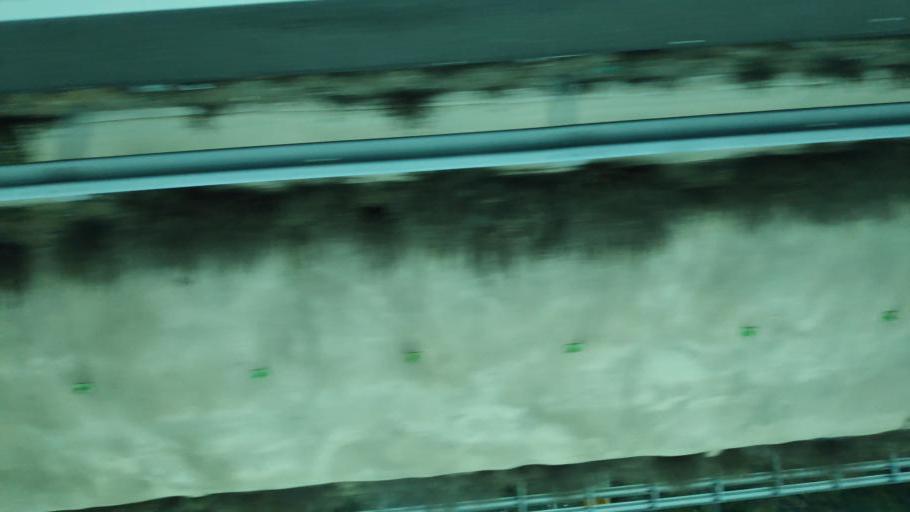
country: ES
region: Castille-La Mancha
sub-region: Provincia de Cuenca
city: Tarancon
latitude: 40.0169
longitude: -3.0328
